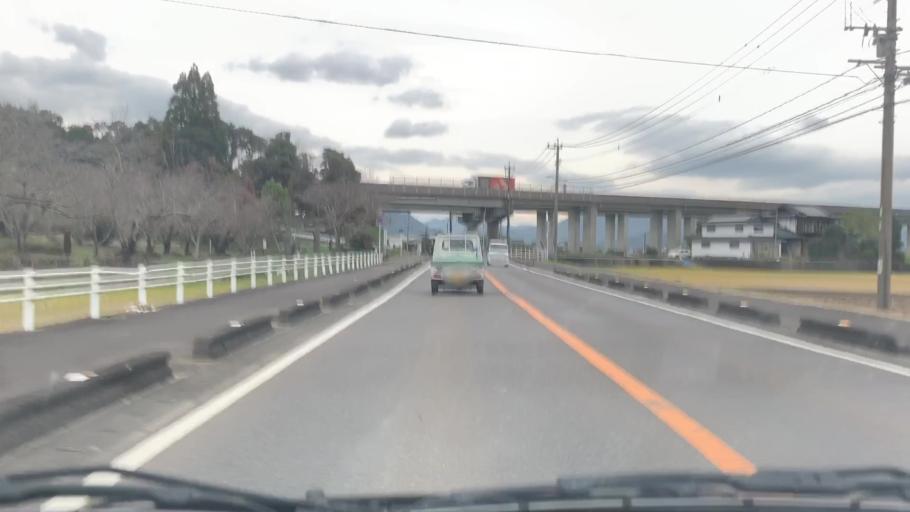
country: JP
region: Saga Prefecture
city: Takeocho-takeo
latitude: 33.1762
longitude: 130.0470
